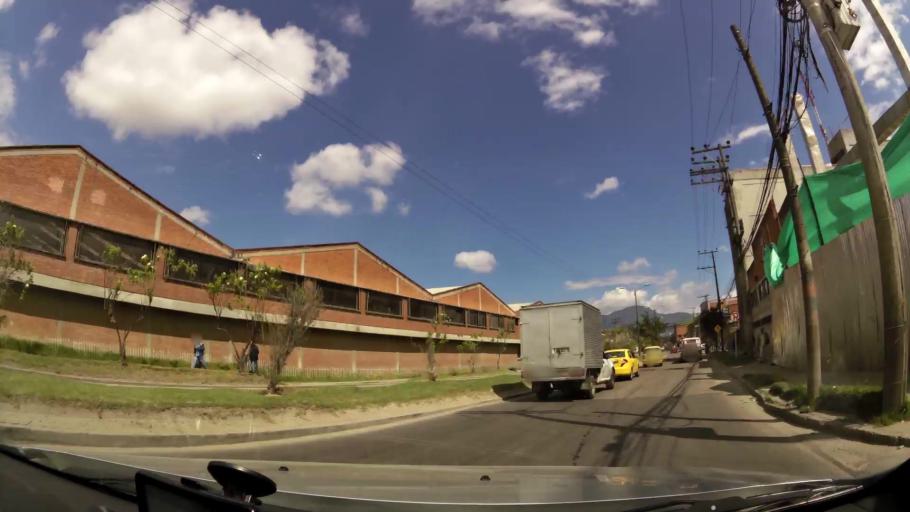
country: CO
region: Bogota D.C.
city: Bogota
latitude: 4.6367
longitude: -74.1128
